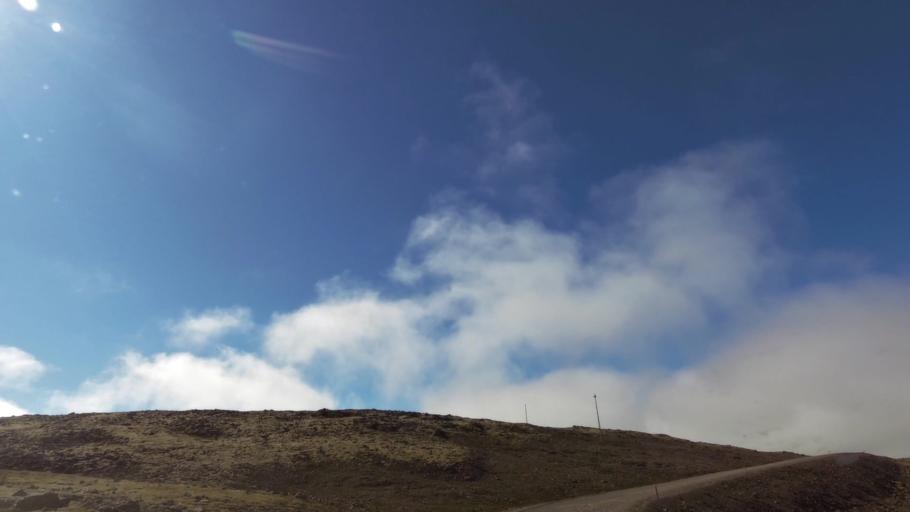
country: IS
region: West
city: Olafsvik
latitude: 65.5536
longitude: -24.2266
